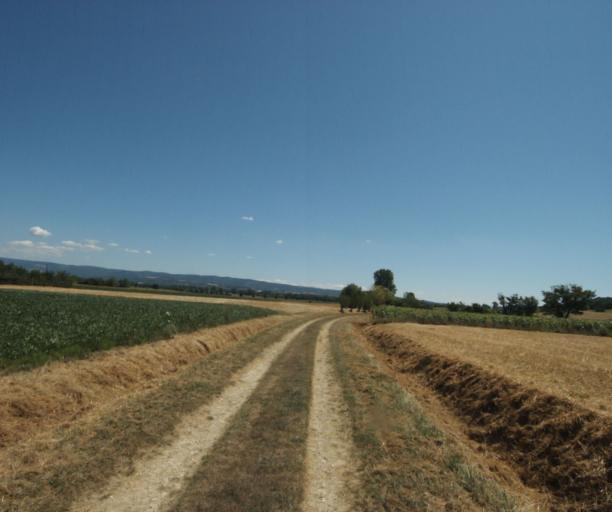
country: FR
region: Midi-Pyrenees
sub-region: Departement de la Haute-Garonne
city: Saint-Felix-Lauragais
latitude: 43.4750
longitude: 1.9215
